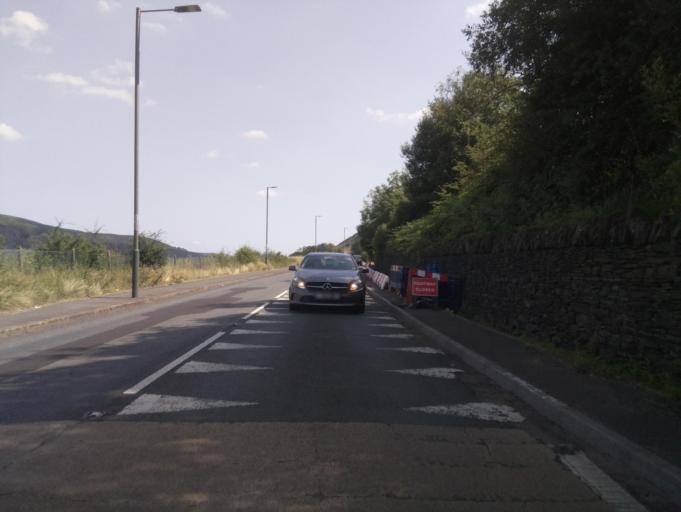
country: GB
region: Wales
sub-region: Caerphilly County Borough
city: Rhymney
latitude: 51.7398
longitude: -3.2738
